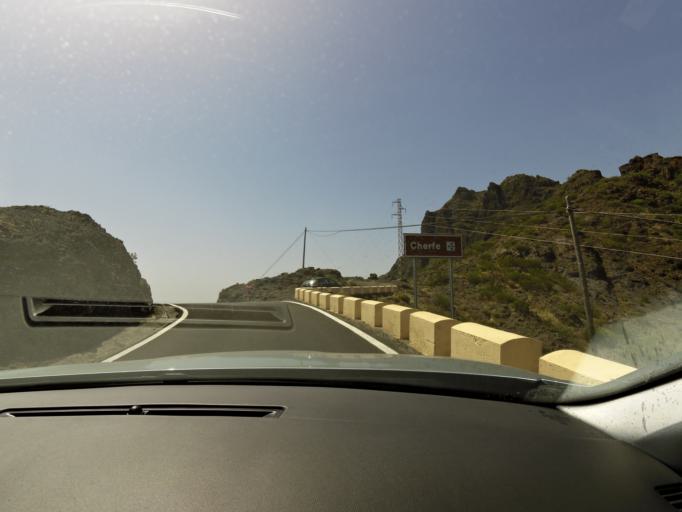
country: ES
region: Canary Islands
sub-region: Provincia de Santa Cruz de Tenerife
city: Santiago del Teide
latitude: 28.2996
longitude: -16.8237
